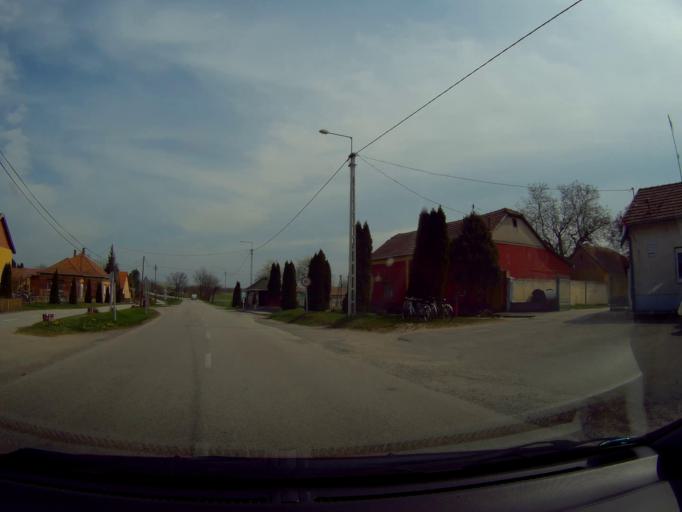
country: HU
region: Bacs-Kiskun
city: Helvecia
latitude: 46.7580
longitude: 19.6018
